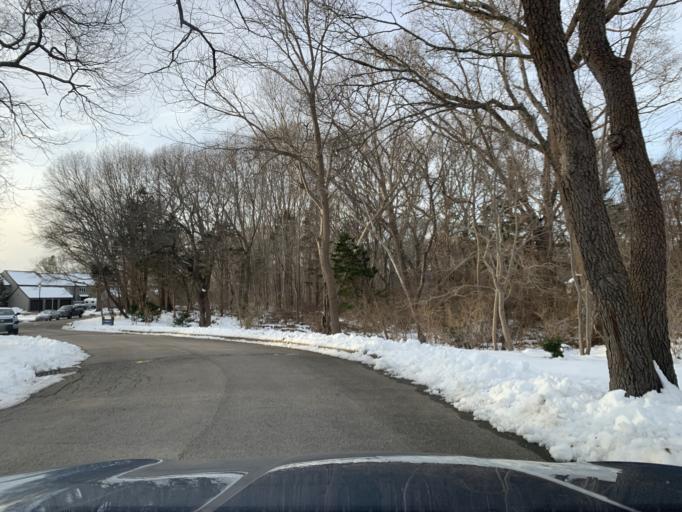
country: US
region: Rhode Island
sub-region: Washington County
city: North Kingstown
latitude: 41.5845
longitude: -71.4364
